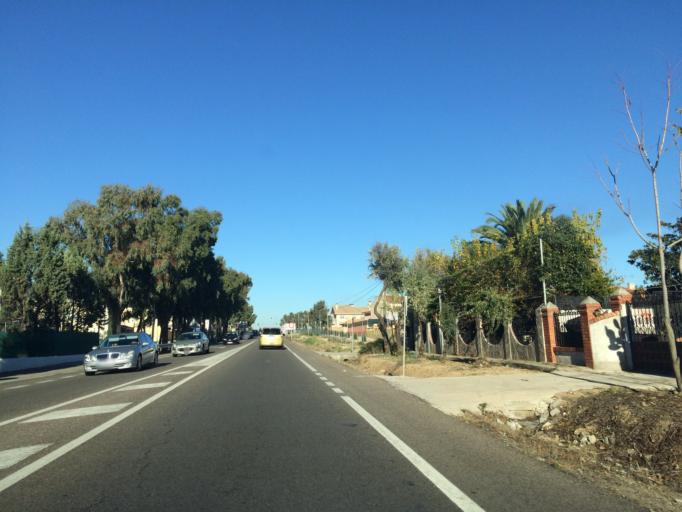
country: ES
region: Madrid
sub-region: Provincia de Madrid
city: Serranillos del Valle
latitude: 40.1825
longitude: -3.8855
